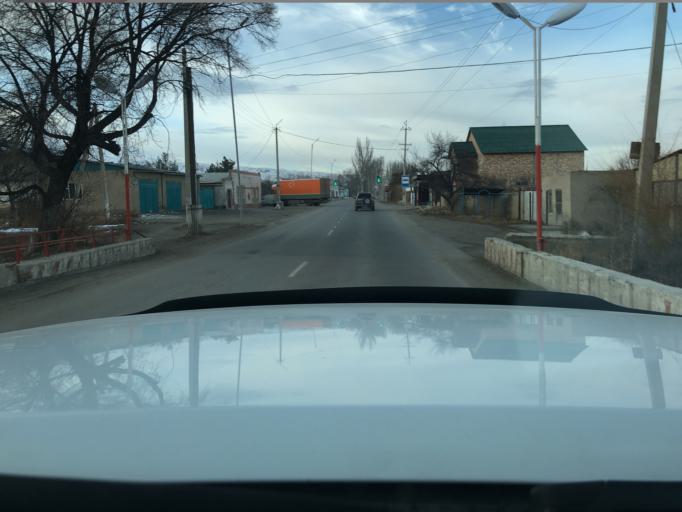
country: KG
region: Ysyk-Koel
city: Karakol
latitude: 42.4739
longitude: 78.3880
